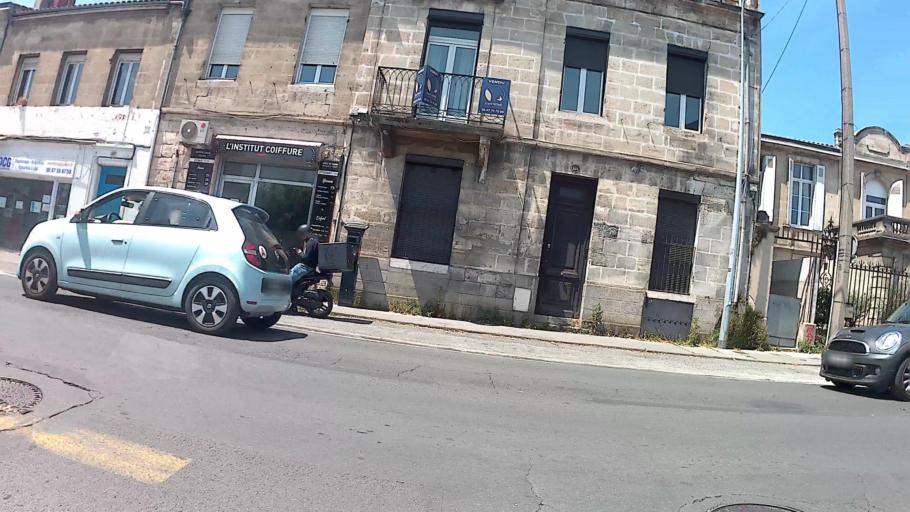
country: FR
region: Aquitaine
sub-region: Departement de la Gironde
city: Talence
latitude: 44.8147
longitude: -0.5797
